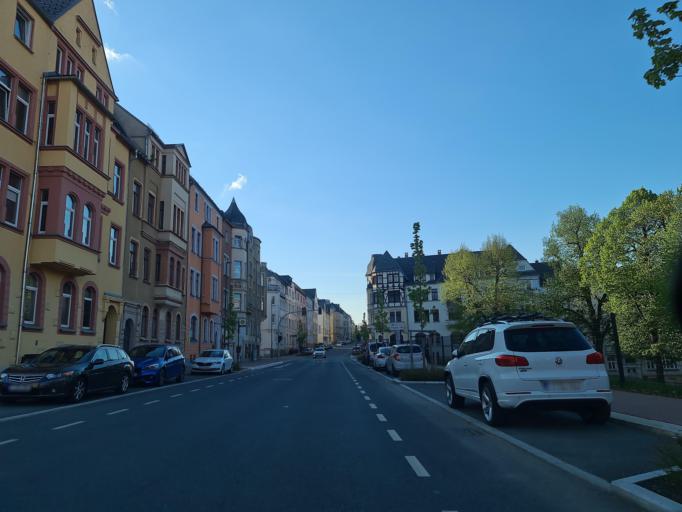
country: DE
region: Saxony
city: Auerbach
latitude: 50.5061
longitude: 12.3949
